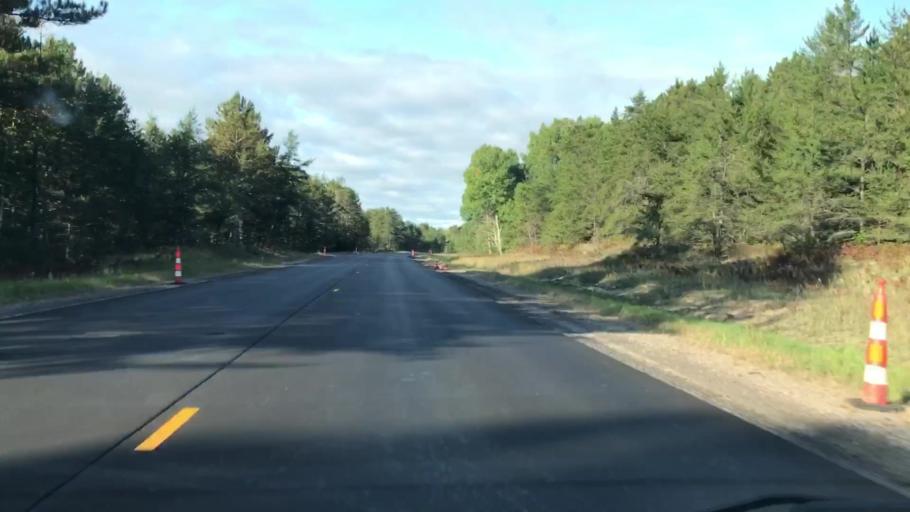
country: US
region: Michigan
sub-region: Mackinac County
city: Saint Ignace
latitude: 46.3483
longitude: -84.9140
